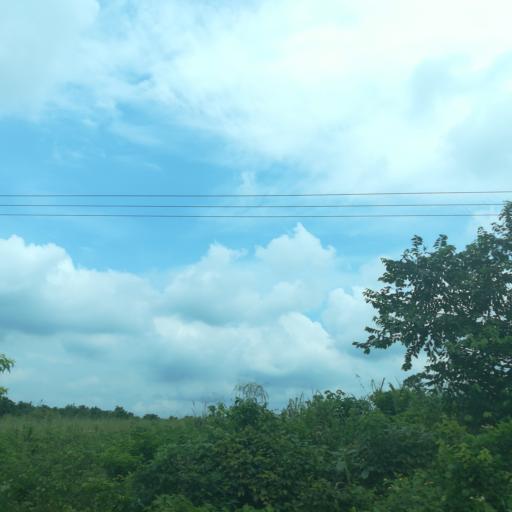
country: NG
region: Lagos
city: Ejirin
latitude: 6.6545
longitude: 3.7218
